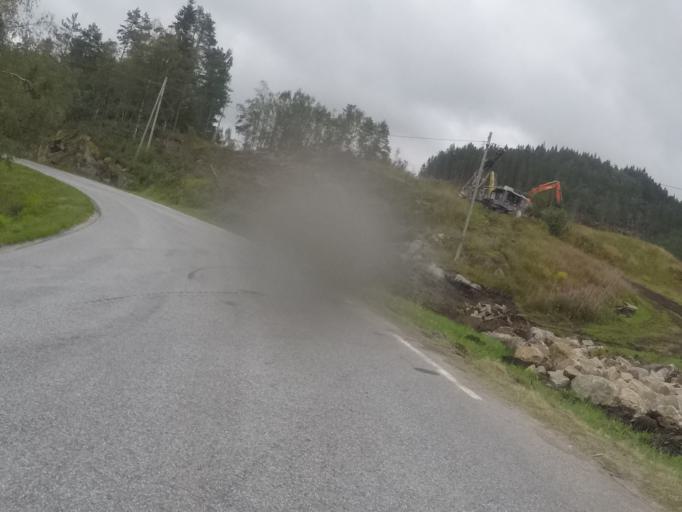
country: NO
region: Vest-Agder
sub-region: Audnedal
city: Konsmo
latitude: 58.2777
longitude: 7.3904
